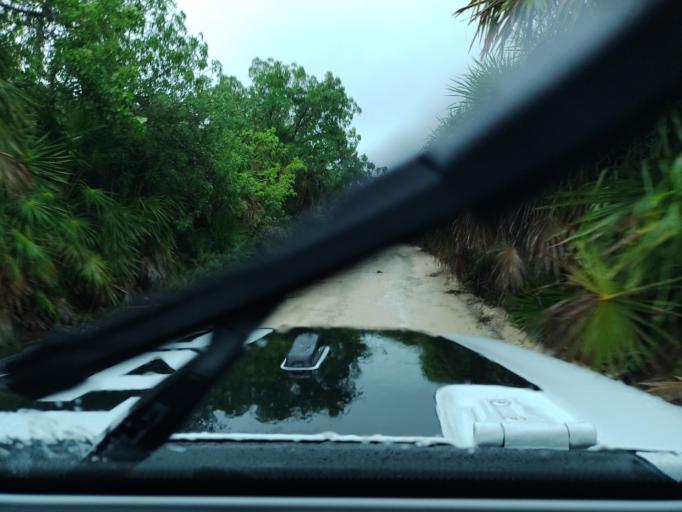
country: MX
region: Quintana Roo
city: Tulum
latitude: 19.9315
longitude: -87.4529
